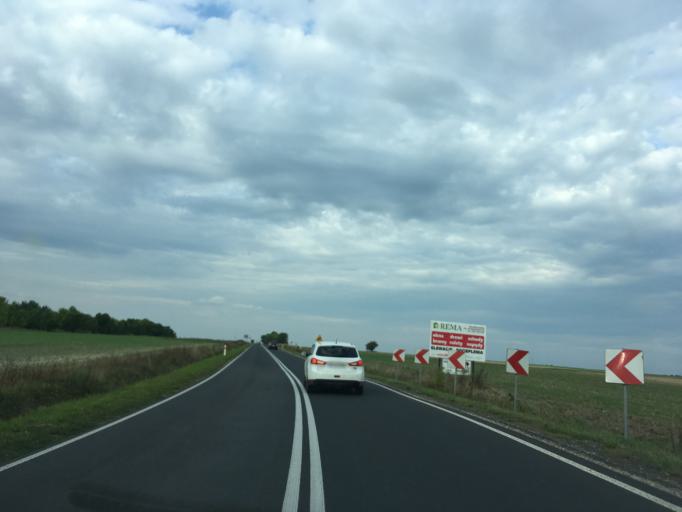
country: PL
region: Swietokrzyskie
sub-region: Powiat wloszczowski
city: Wloszczowa
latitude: 50.8304
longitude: 19.9544
